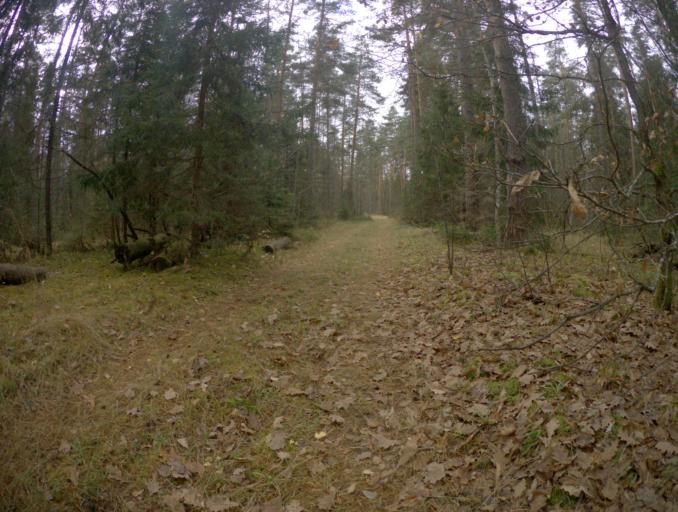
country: RU
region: Vladimir
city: Orgtrud
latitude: 56.1129
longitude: 40.6198
